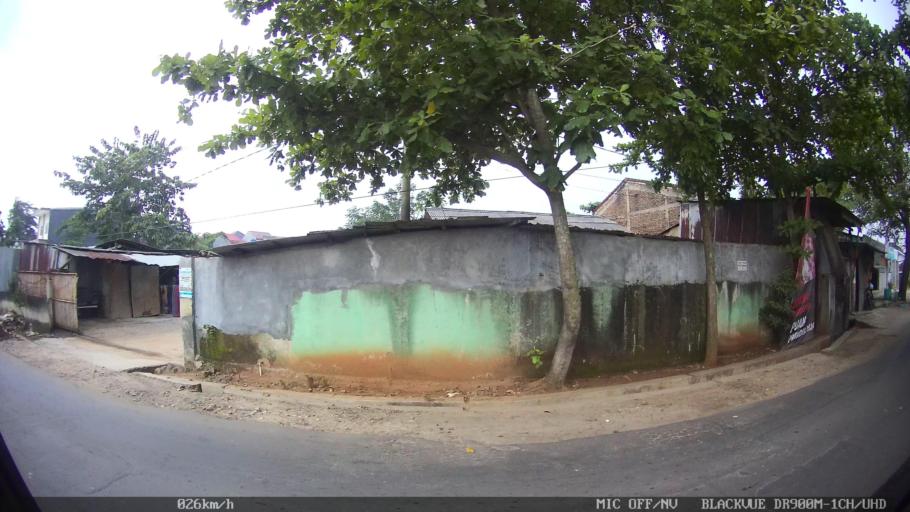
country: ID
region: Lampung
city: Bandarlampung
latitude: -5.4157
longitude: 105.2849
